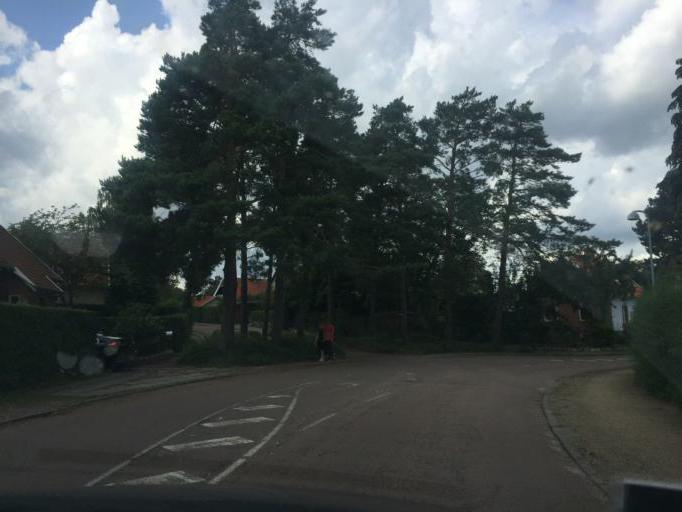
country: DK
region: Capital Region
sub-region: Rudersdal Kommune
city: Holte
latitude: 55.7929
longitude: 12.4503
